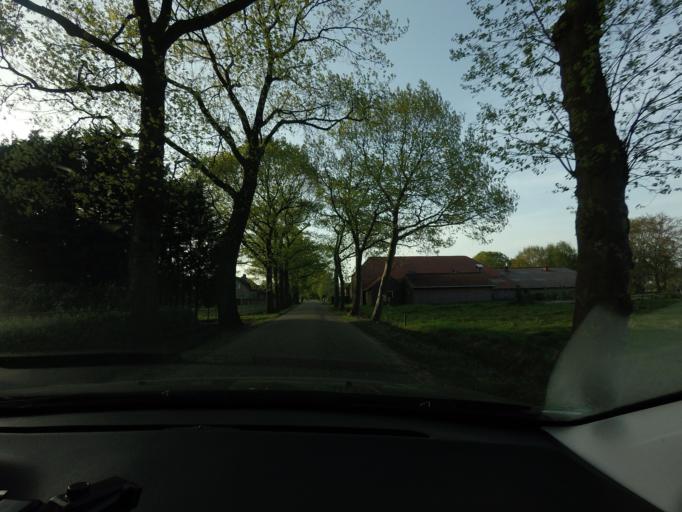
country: NL
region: North Brabant
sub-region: Gemeente Baarle-Nassau
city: Baarle-Nassau
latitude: 51.5027
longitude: 4.9744
